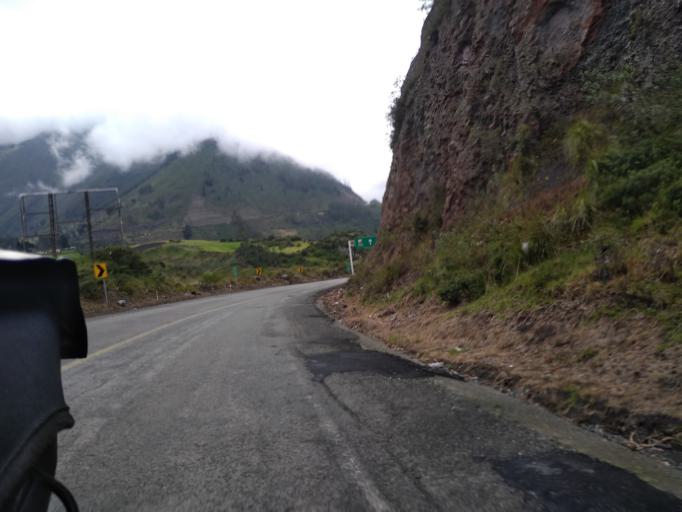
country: EC
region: Tungurahua
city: Banos
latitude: -1.5065
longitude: -78.5197
